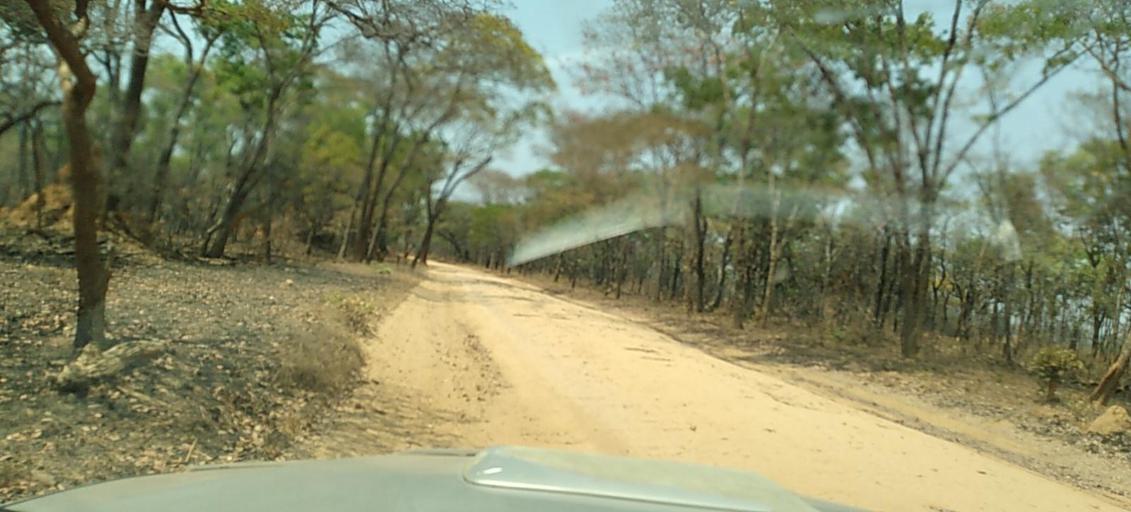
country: ZM
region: North-Western
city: Kasempa
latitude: -13.6090
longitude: 26.1895
